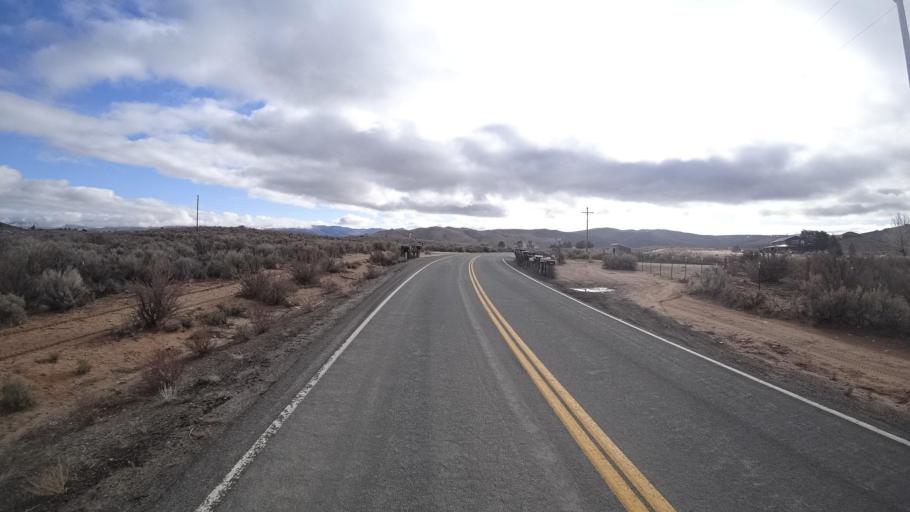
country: US
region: Nevada
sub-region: Washoe County
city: Cold Springs
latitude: 39.8695
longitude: -119.9537
